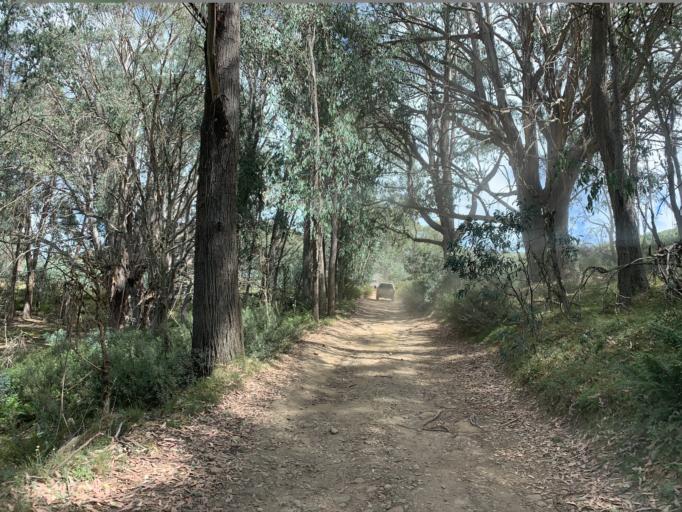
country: AU
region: Victoria
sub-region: Mansfield
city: Mansfield
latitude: -37.1090
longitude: 146.5342
